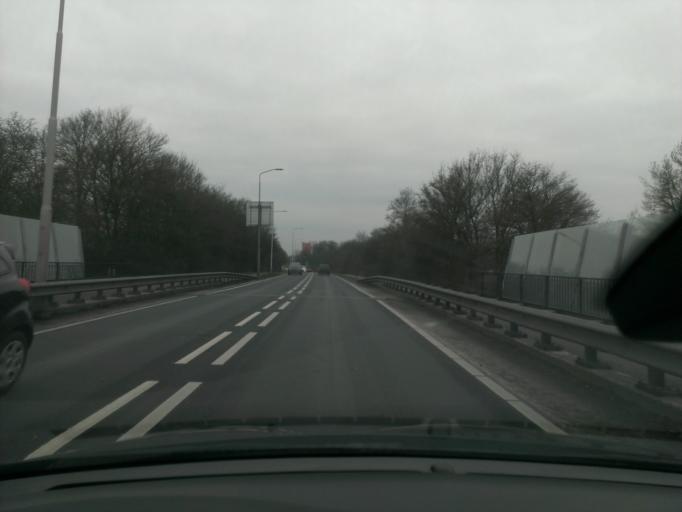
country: NL
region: Overijssel
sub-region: Gemeente Almelo
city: Almelo
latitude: 52.3622
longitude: 6.6726
